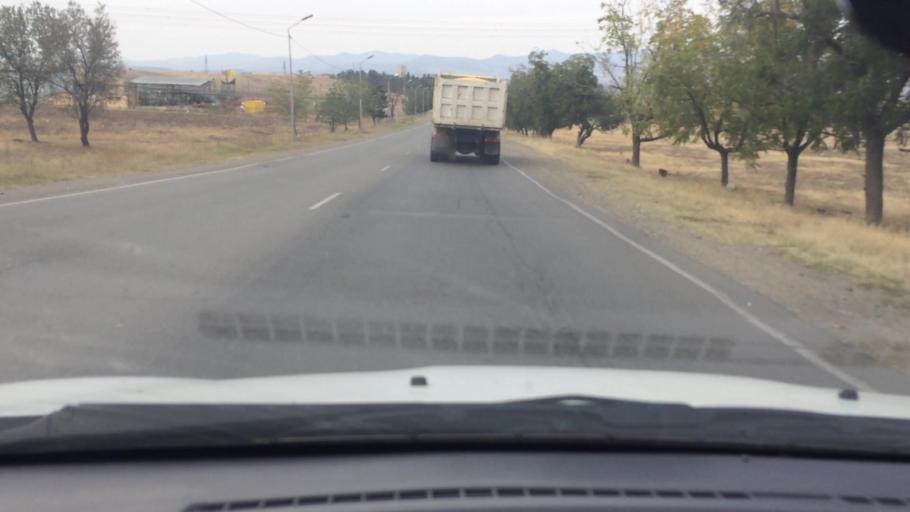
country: GE
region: Kvemo Kartli
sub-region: Marneuli
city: Marneuli
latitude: 41.5176
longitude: 44.7831
